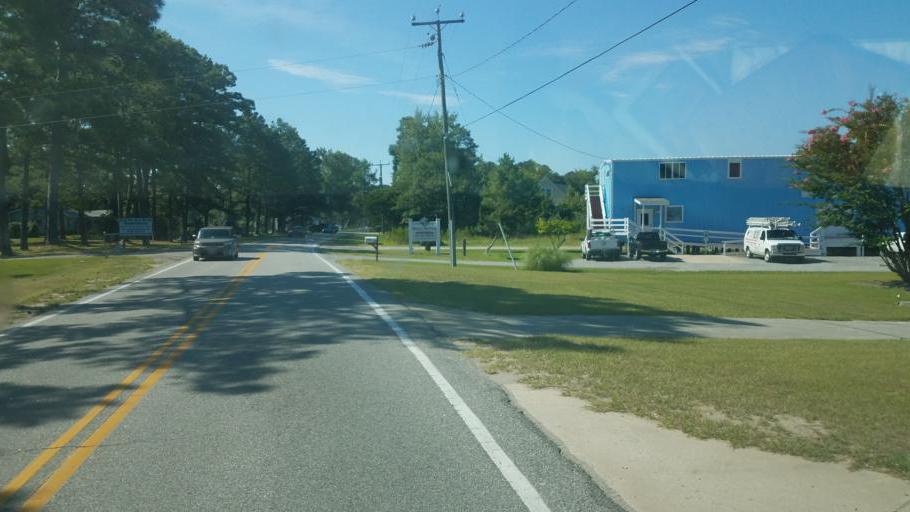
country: US
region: North Carolina
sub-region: Dare County
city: Kill Devil Hills
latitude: 36.0138
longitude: -75.6940
